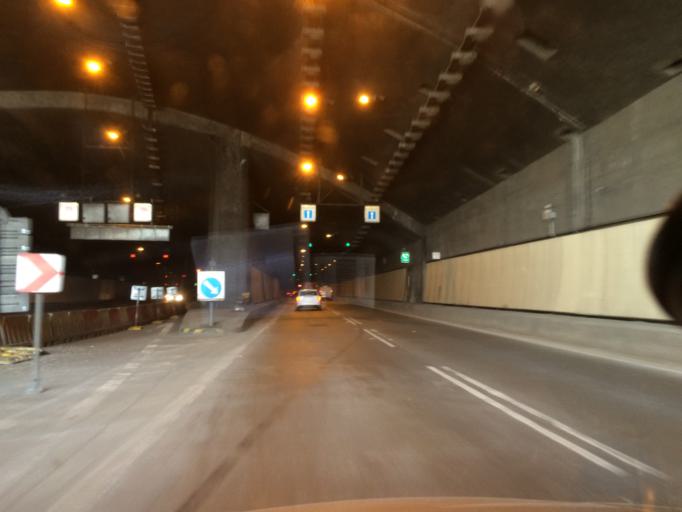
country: CZ
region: Praha
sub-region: Praha 1
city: Mala Strana
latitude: 50.0867
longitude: 14.3809
